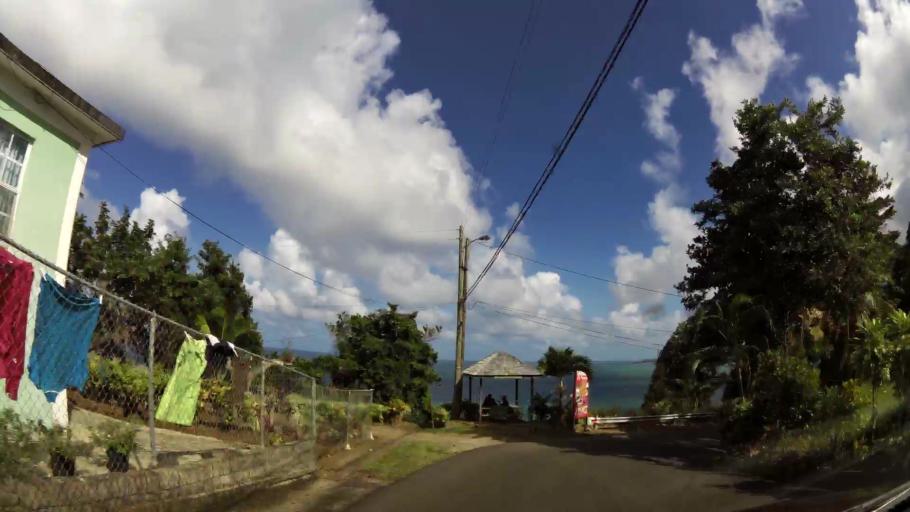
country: DM
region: Saint Andrew
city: Calibishie
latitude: 15.6180
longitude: -61.4075
